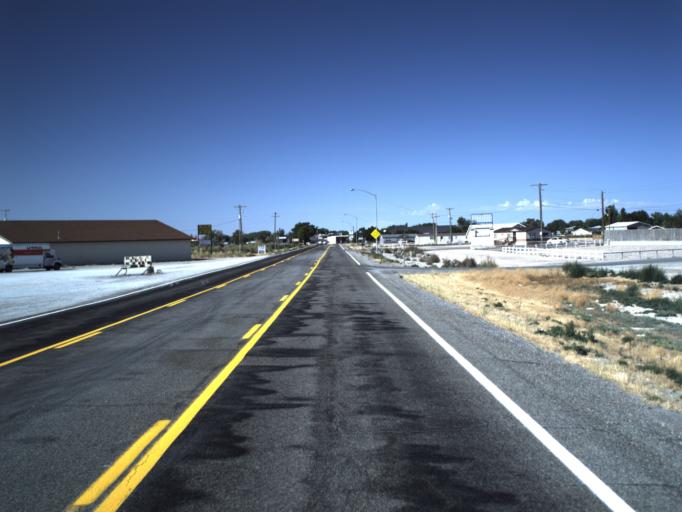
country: US
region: Utah
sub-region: Millard County
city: Delta
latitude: 39.3580
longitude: -112.5582
